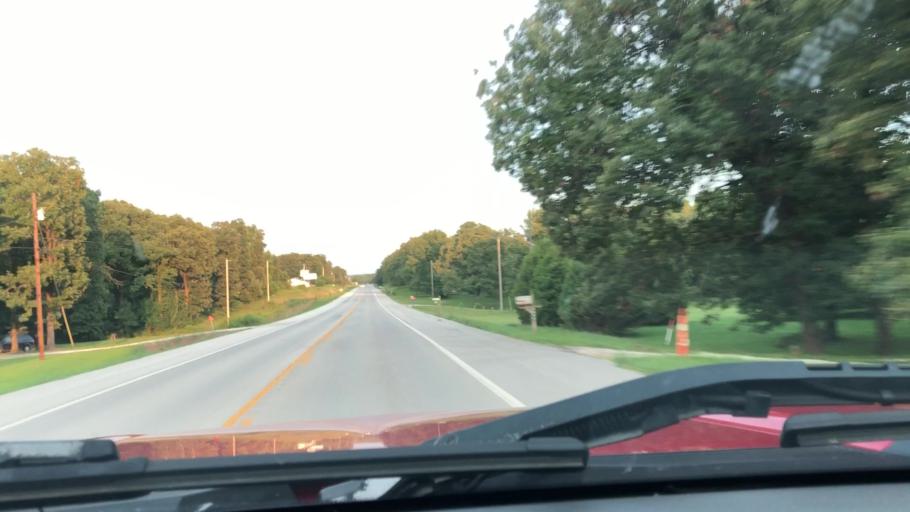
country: US
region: Missouri
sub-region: Jasper County
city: Duquesne
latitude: 36.9747
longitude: -94.4580
